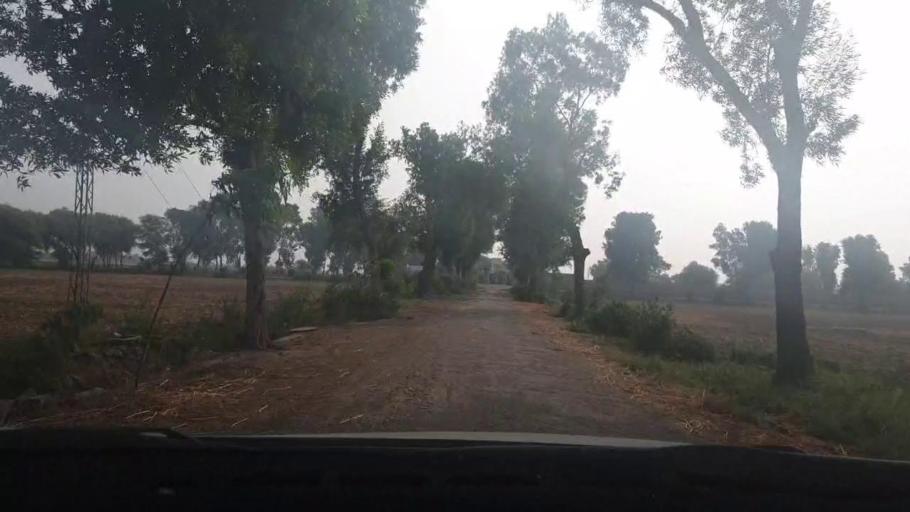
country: PK
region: Sindh
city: Tando Muhammad Khan
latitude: 25.1100
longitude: 68.5419
